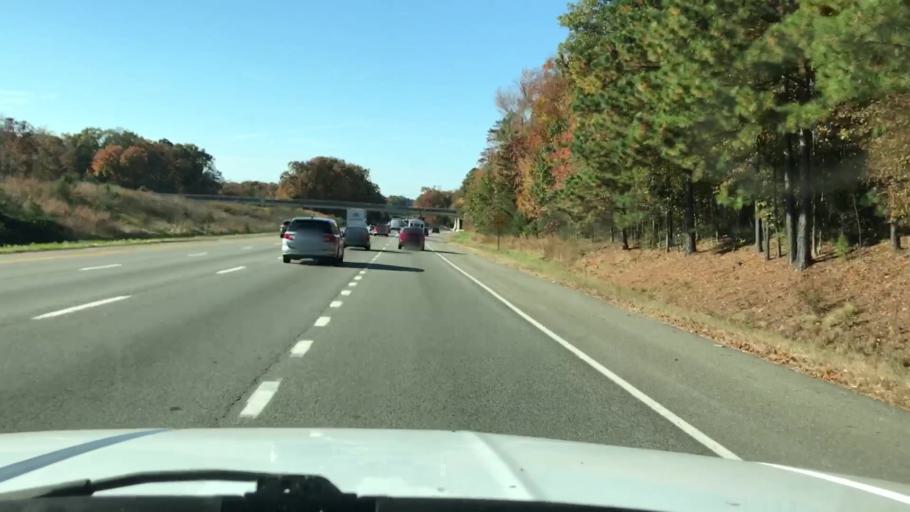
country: US
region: Virginia
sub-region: Henrico County
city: Tuckahoe
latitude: 37.6308
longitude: -77.5665
